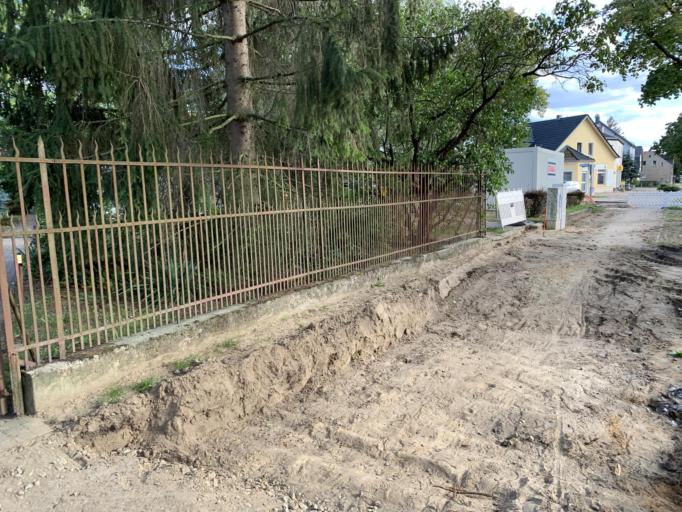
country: DE
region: Brandenburg
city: Petershagen
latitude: 52.5238
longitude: 13.7541
